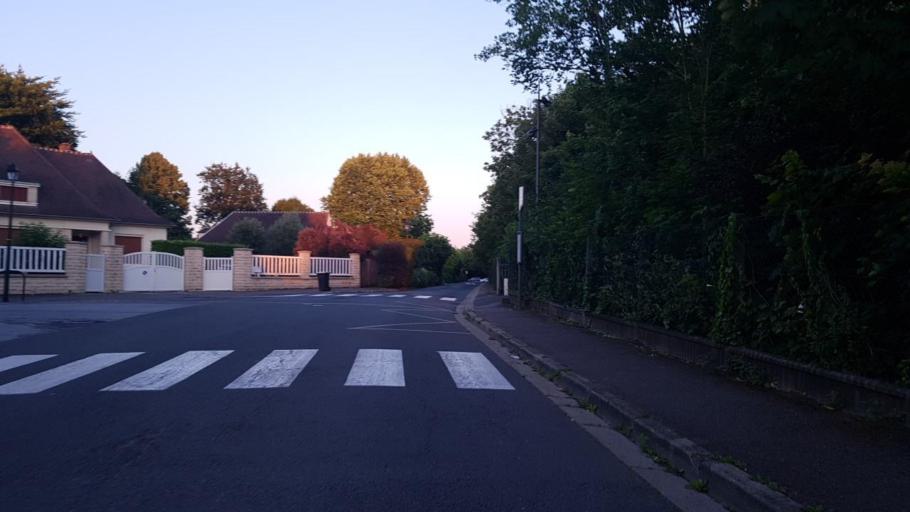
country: FR
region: Picardie
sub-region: Departement de l'Oise
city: Senlis
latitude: 49.2095
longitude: 2.5884
